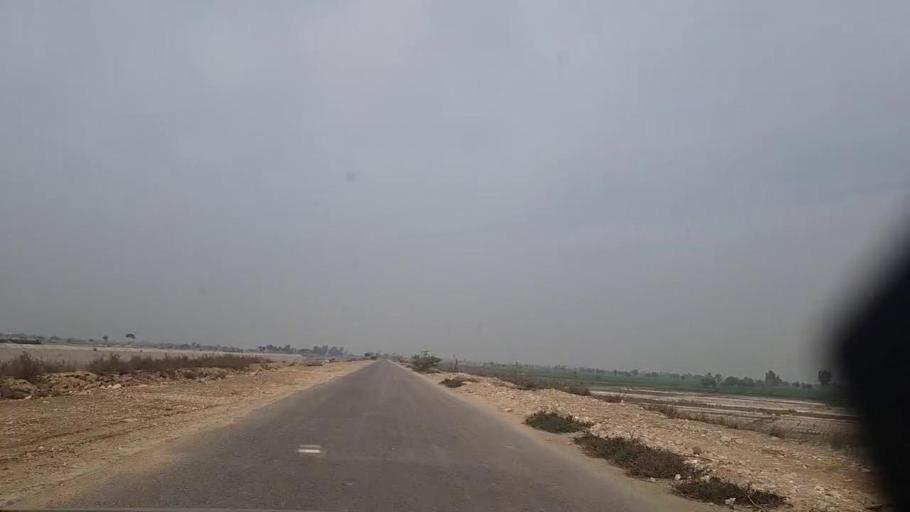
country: PK
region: Sindh
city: Sakrand
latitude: 26.2747
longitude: 68.2322
